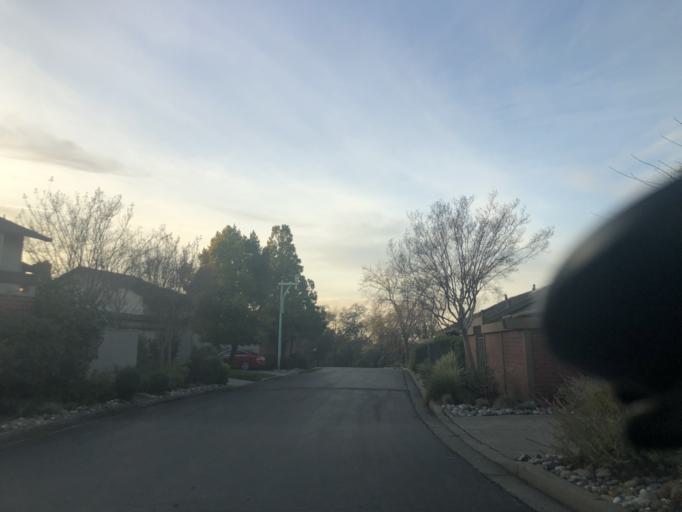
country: US
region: California
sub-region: Sacramento County
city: Gold River
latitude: 38.6375
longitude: -121.2322
